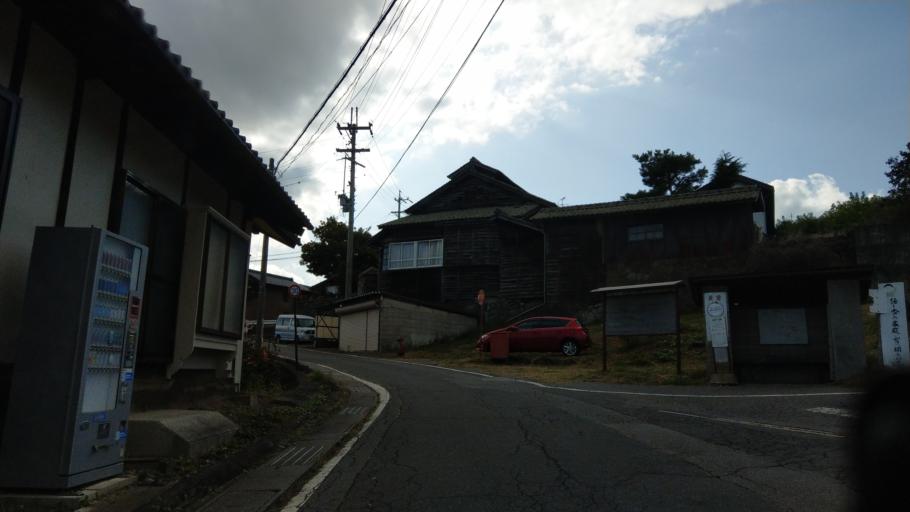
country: JP
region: Nagano
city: Komoro
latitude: 36.3489
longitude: 138.4120
